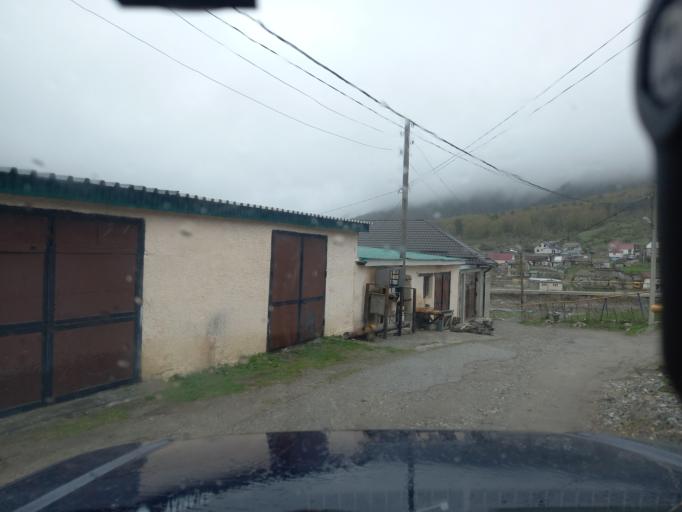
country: RU
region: Kabardino-Balkariya
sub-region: El'brusskiy Rayon
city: El'brus
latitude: 43.2612
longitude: 42.6490
